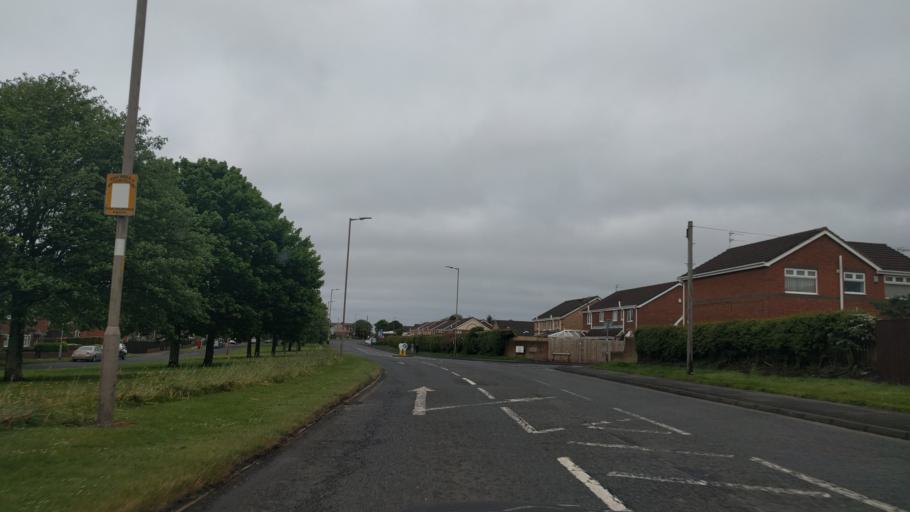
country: GB
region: England
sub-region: Northumberland
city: Choppington
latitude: 55.1591
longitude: -1.6097
